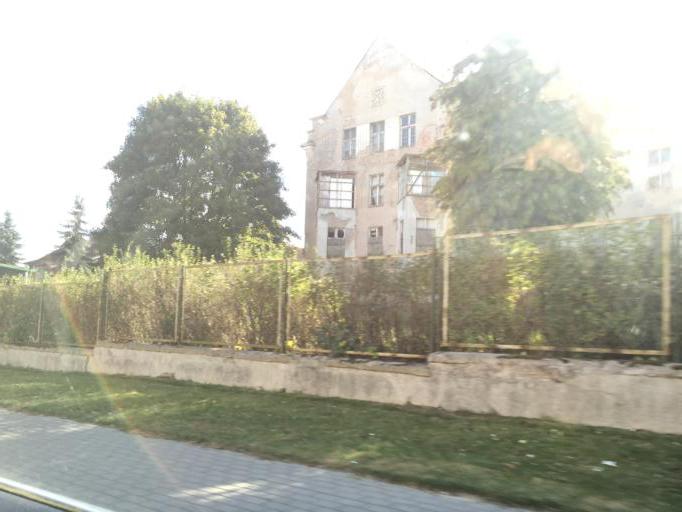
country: PL
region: Warmian-Masurian Voivodeship
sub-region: Powiat bartoszycki
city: Bartoszyce
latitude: 54.2462
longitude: 20.8132
